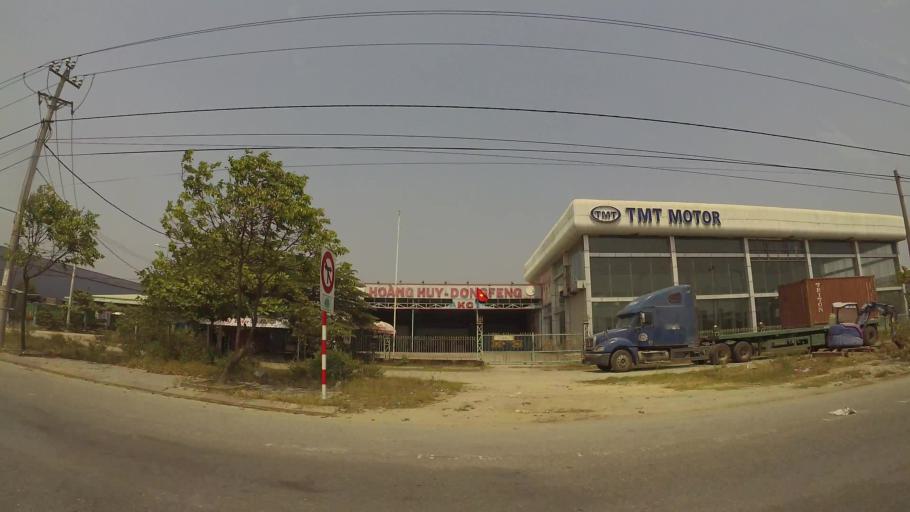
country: VN
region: Da Nang
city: Cam Le
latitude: 15.9886
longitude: 108.1989
